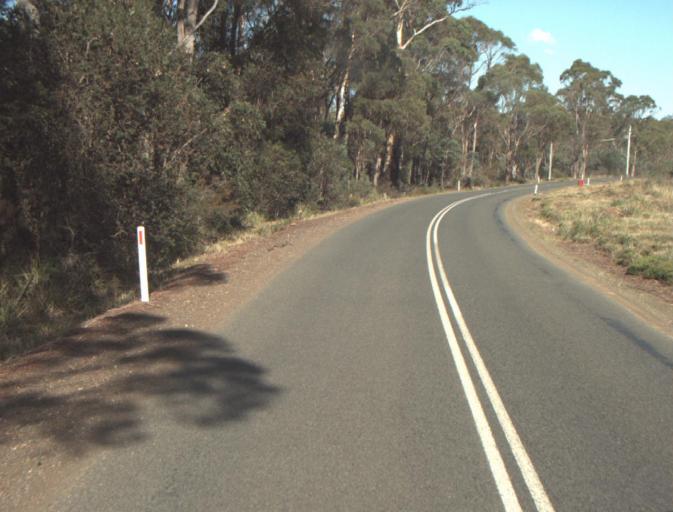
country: AU
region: Tasmania
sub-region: Launceston
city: Mayfield
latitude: -41.3279
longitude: 147.1396
